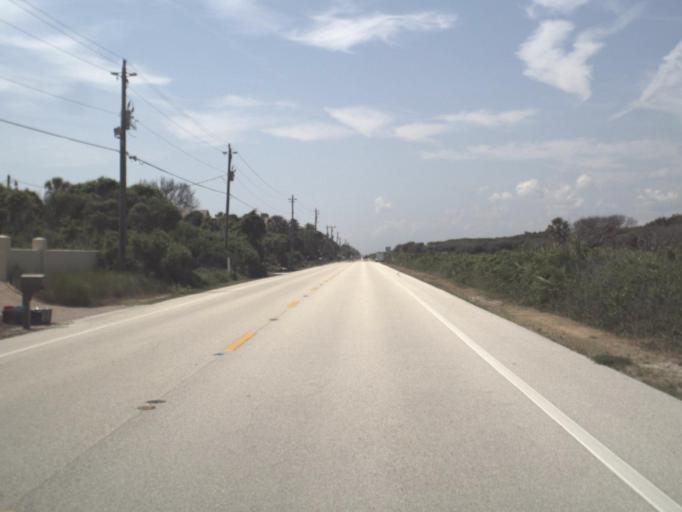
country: US
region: Florida
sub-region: Saint Johns County
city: Palm Valley
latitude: 30.0666
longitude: -81.3336
